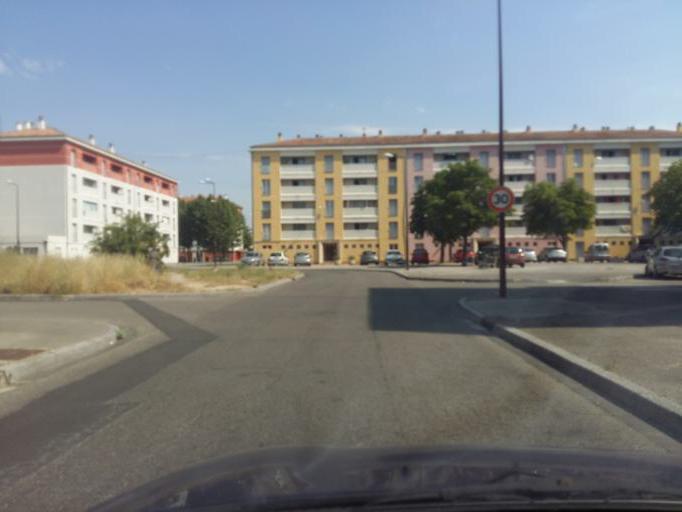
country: FR
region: Provence-Alpes-Cote d'Azur
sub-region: Departement du Vaucluse
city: Montfavet
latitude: 43.9334
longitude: 4.8702
